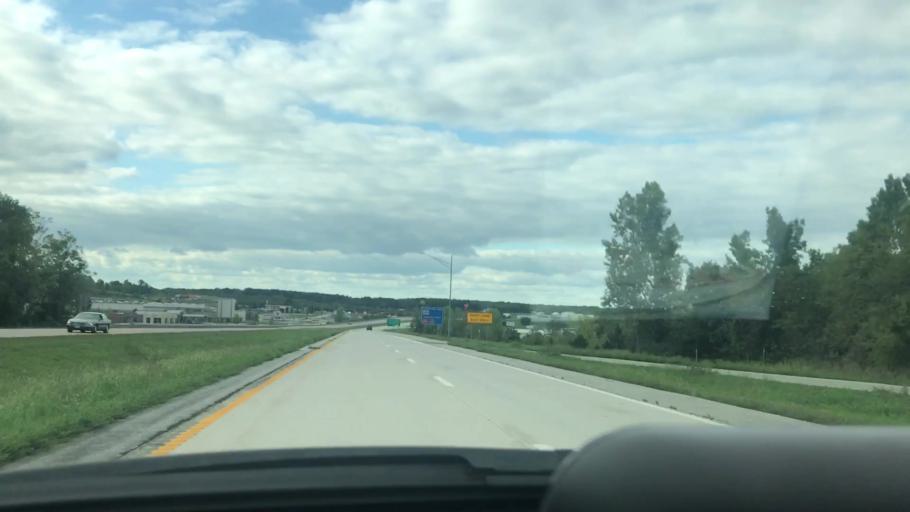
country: US
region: Missouri
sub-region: Benton County
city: Warsaw
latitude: 38.2560
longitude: -93.3655
